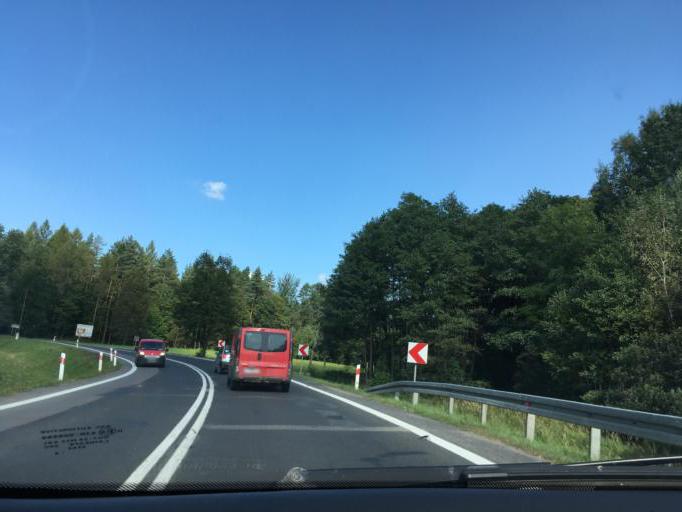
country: PL
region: Subcarpathian Voivodeship
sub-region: Powiat sanocki
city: Zagorz
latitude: 49.5092
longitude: 22.2932
